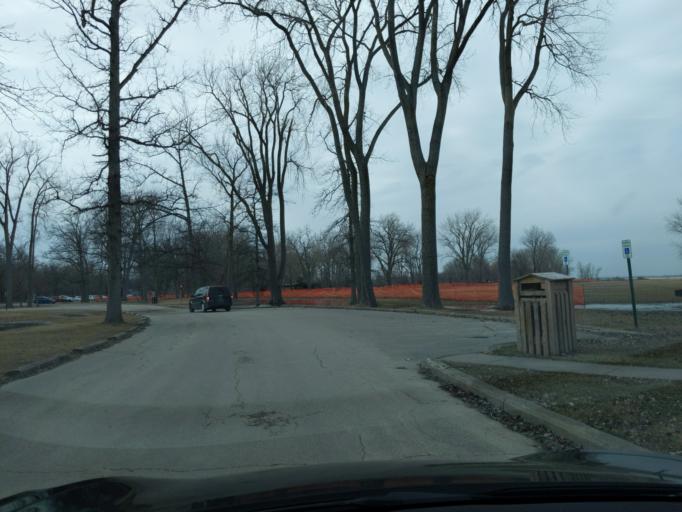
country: US
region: Michigan
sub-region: Bay County
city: Bay City
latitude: 43.6676
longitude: -83.9050
